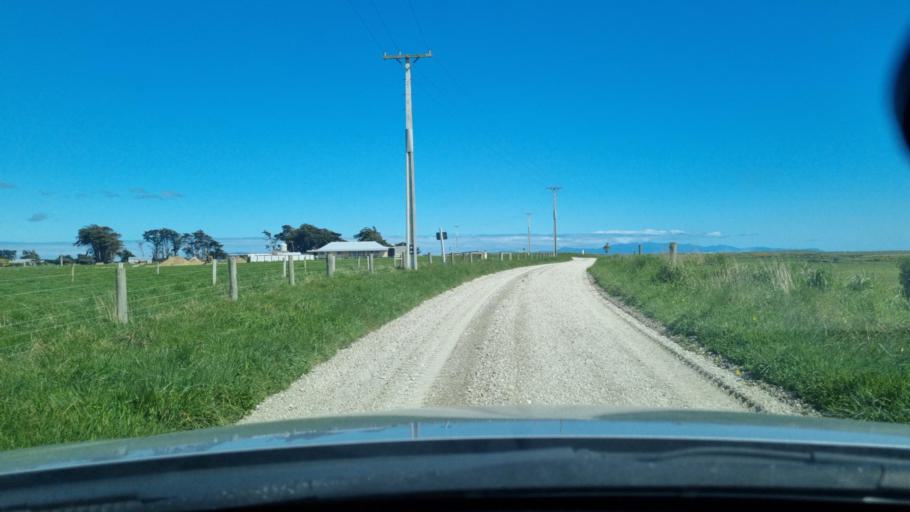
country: NZ
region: Southland
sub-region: Invercargill City
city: Invercargill
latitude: -46.3982
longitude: 168.2572
